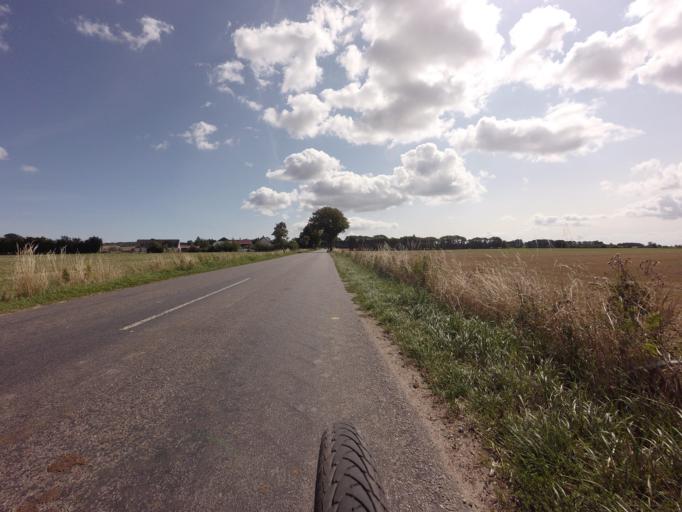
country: DK
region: Zealand
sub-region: Vordingborg Kommune
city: Stege
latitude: 54.9745
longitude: 12.4495
